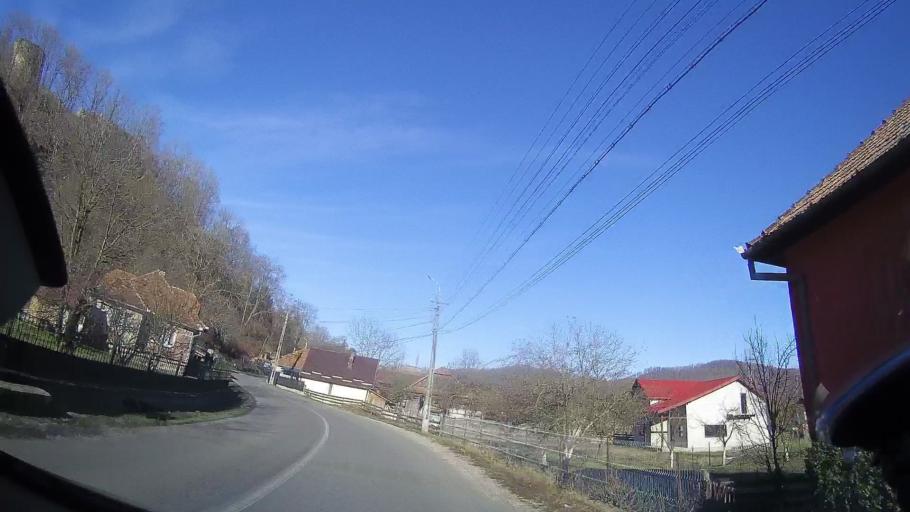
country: RO
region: Cluj
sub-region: Comuna Poeni
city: Poeni
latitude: 46.8800
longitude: 22.8797
